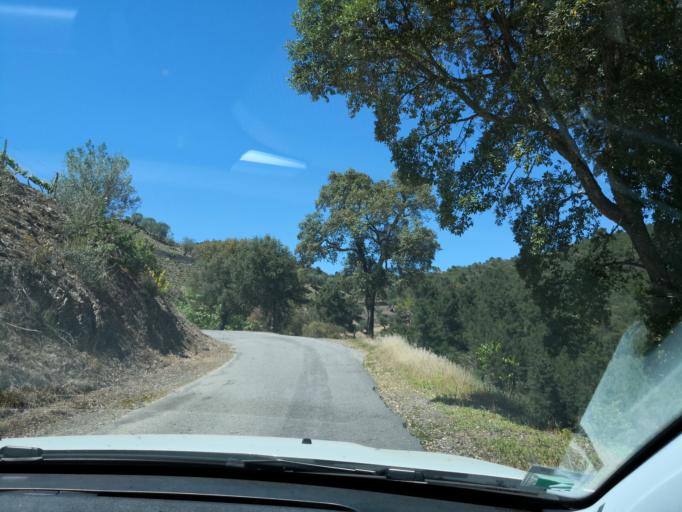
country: PT
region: Vila Real
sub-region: Vila Real
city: Vila Real
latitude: 41.2325
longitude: -7.7194
